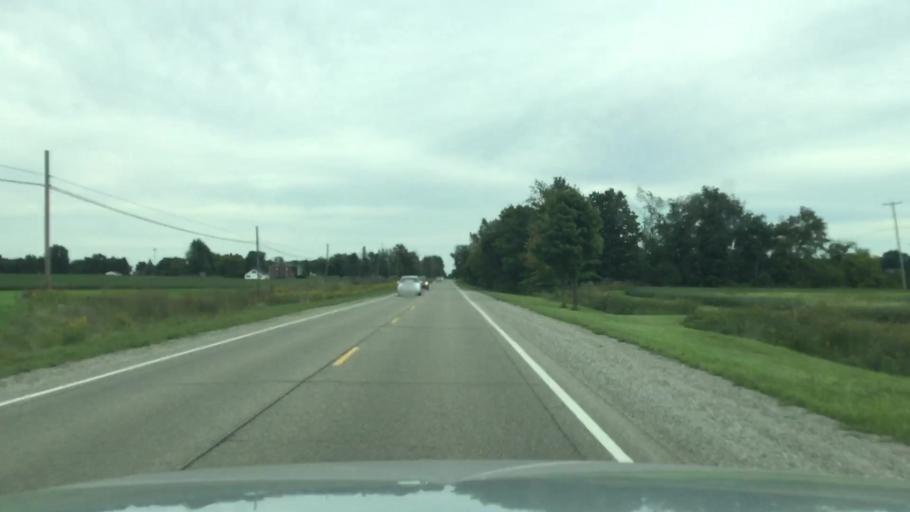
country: US
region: Michigan
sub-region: Genesee County
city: Swartz Creek
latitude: 42.9570
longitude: -83.8789
